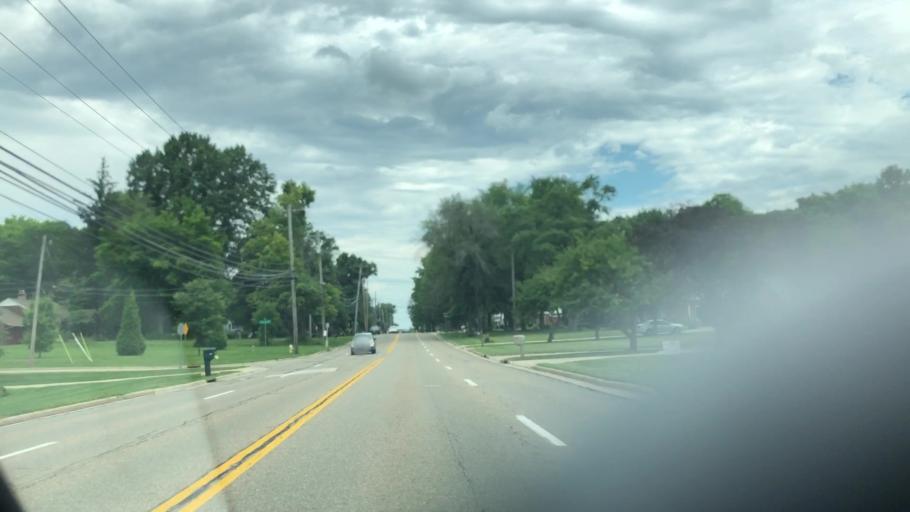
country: US
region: Ohio
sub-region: Summit County
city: Fairlawn
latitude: 41.1190
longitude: -81.6098
